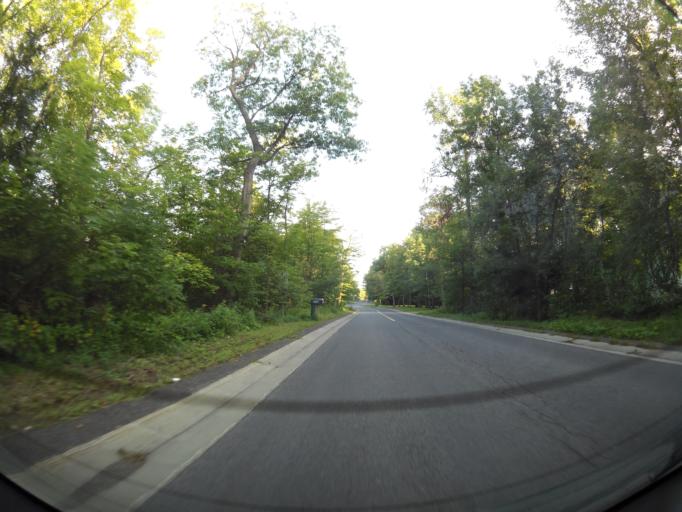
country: CA
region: Ontario
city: Clarence-Rockland
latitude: 45.5048
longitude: -75.4226
